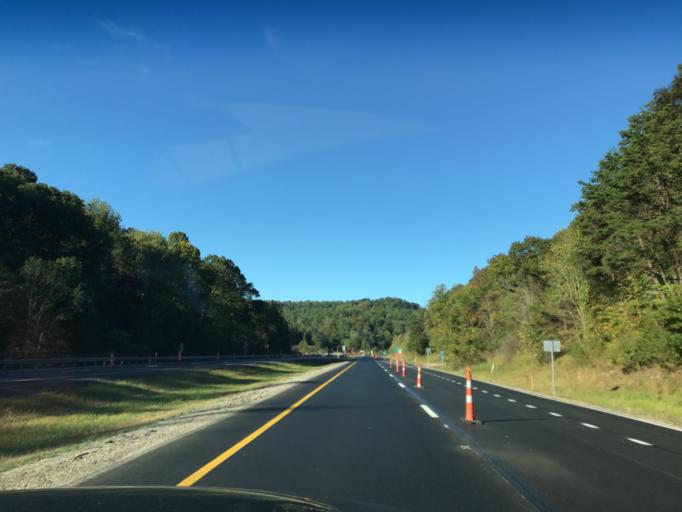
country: US
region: Ohio
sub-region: Washington County
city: Reno
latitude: 39.2471
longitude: -81.3597
